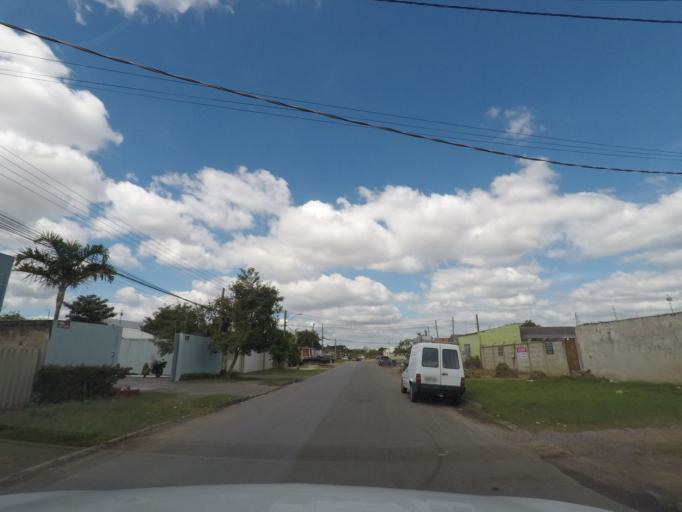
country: BR
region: Parana
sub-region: Sao Jose Dos Pinhais
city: Sao Jose dos Pinhais
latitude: -25.5099
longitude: -49.2178
